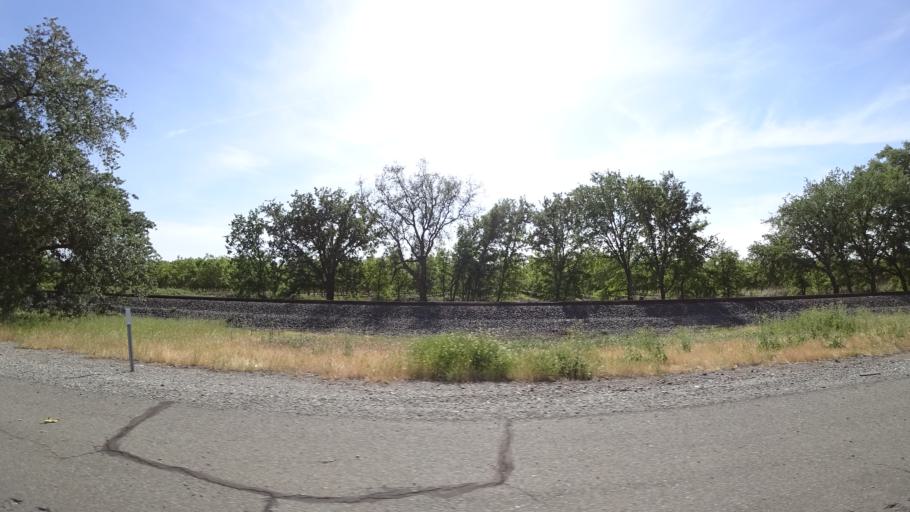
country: US
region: California
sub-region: Tehama County
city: Los Molinos
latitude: 39.9616
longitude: -122.0695
